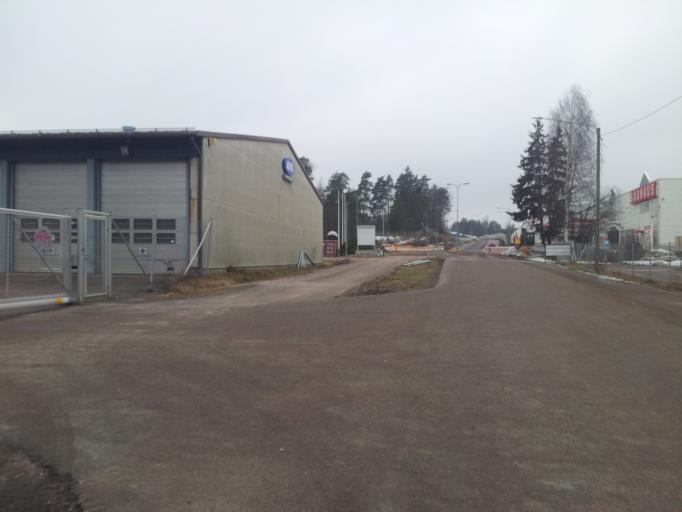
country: FI
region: Uusimaa
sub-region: Helsinki
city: Koukkuniemi
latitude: 60.1588
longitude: 24.7151
